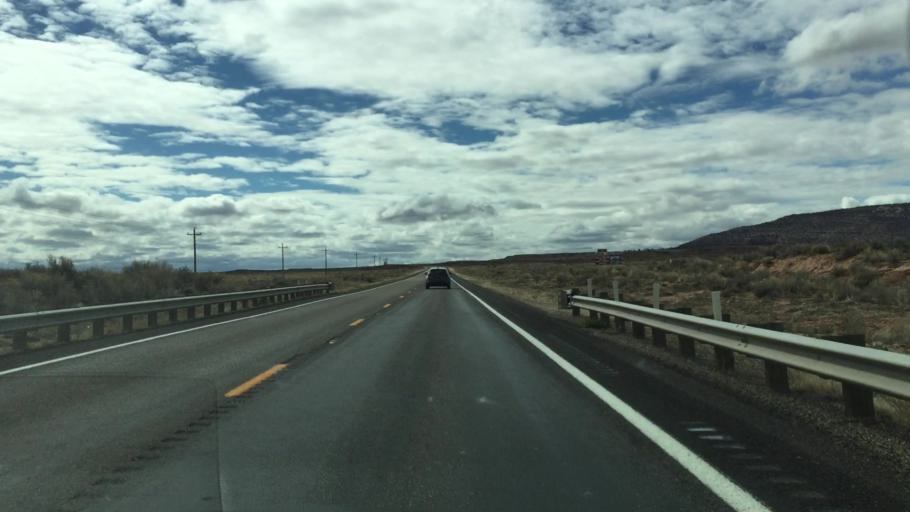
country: US
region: Arizona
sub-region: Coconino County
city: Fredonia
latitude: 36.8667
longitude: -112.6978
